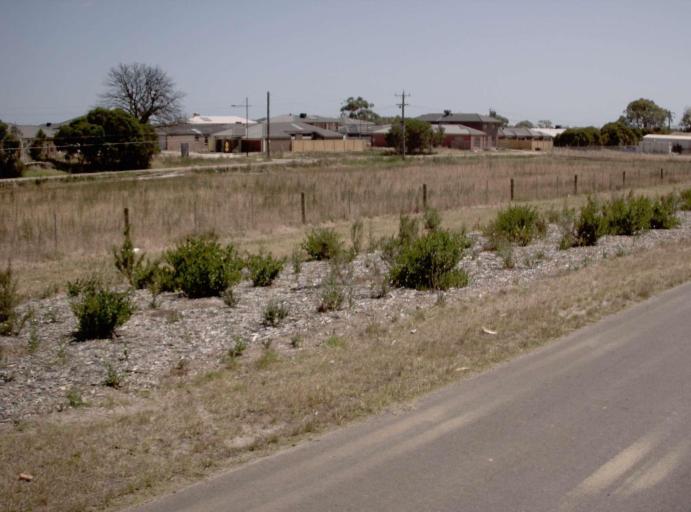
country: AU
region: Victoria
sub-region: Greater Dandenong
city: Keysborough
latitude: -37.9986
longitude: 145.1711
